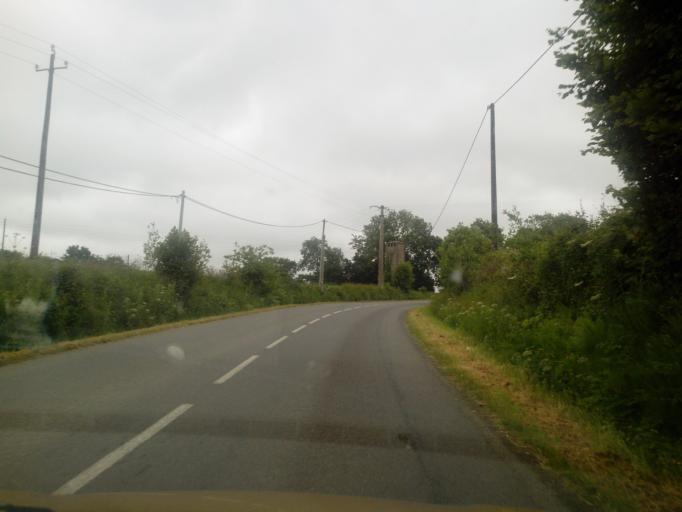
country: FR
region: Brittany
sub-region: Departement d'Ille-et-Vilaine
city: Saint-Ouen-des-Alleux
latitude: 48.3412
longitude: -1.4758
